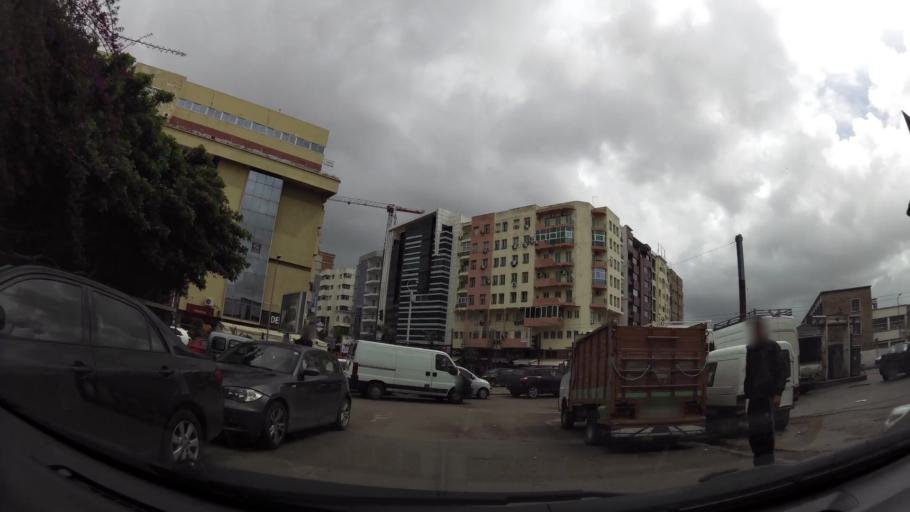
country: MA
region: Grand Casablanca
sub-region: Casablanca
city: Casablanca
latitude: 33.5770
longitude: -7.6262
